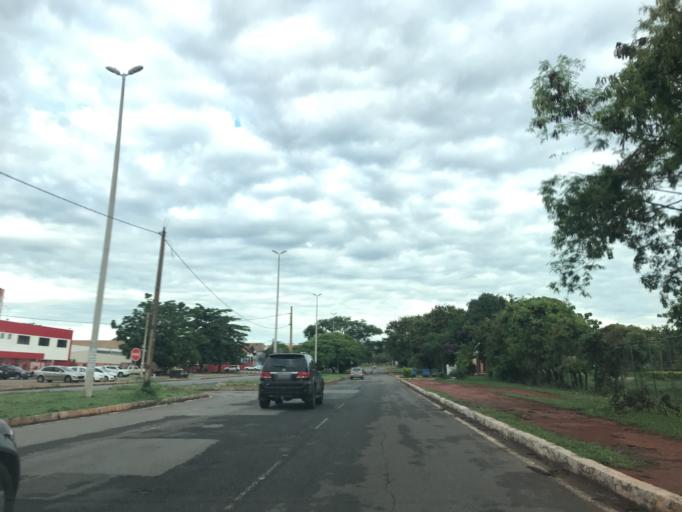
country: BR
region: Federal District
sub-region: Brasilia
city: Brasilia
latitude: -15.8163
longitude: -47.9203
